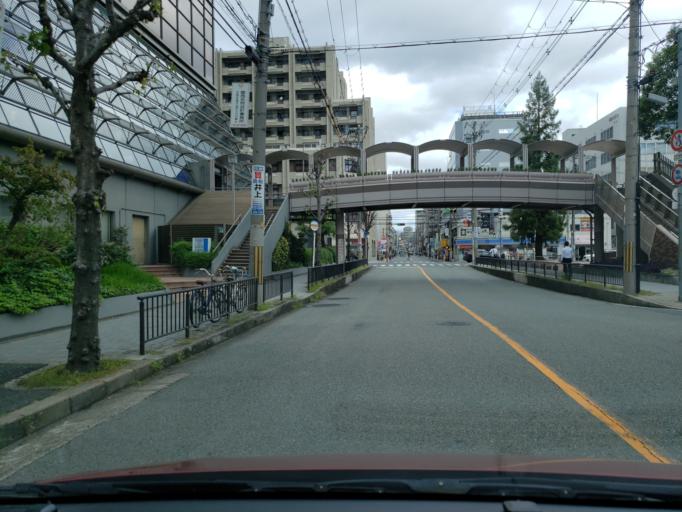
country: JP
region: Osaka
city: Suita
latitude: 34.7592
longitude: 135.4982
